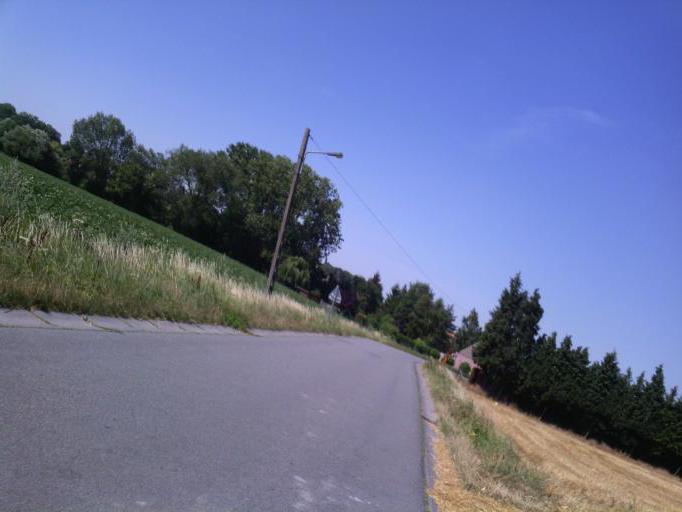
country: BE
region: Wallonia
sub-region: Province du Hainaut
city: Tournai
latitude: 50.6166
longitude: 3.4375
